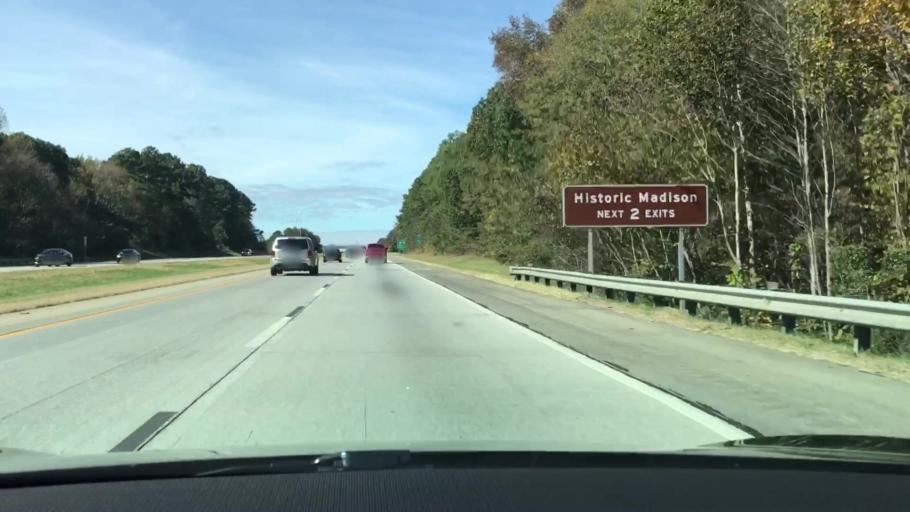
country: US
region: Georgia
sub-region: Morgan County
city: Madison
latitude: 33.5555
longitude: -83.4635
